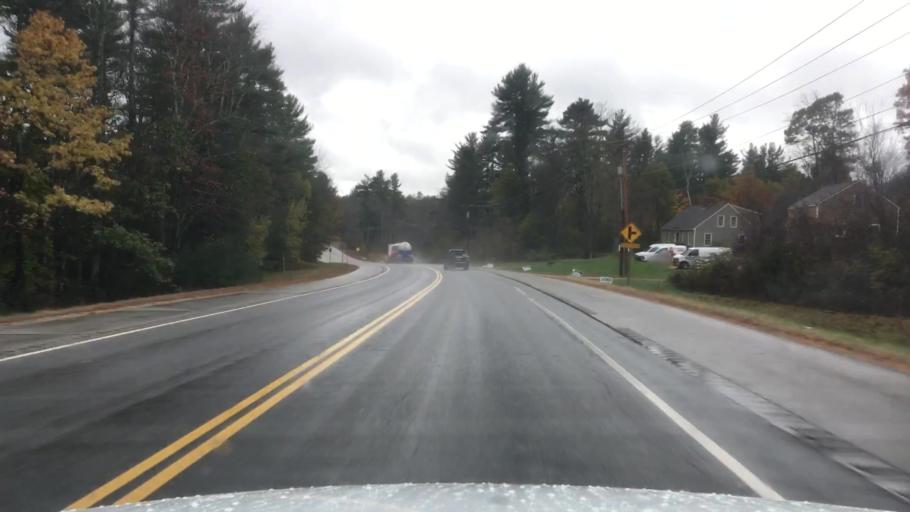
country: US
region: New Hampshire
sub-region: Strafford County
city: Barrington
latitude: 43.2360
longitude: -70.9914
